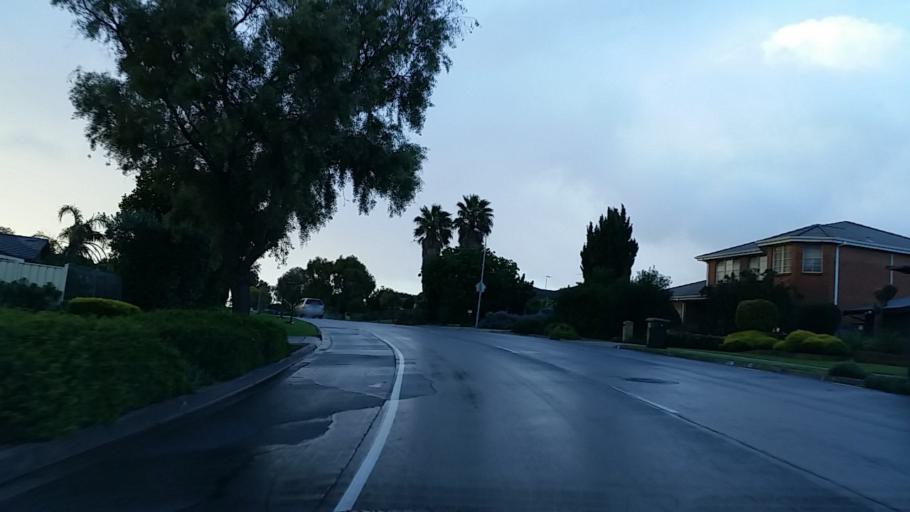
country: AU
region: South Australia
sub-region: Marion
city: Marino
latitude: -35.0653
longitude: 138.5162
